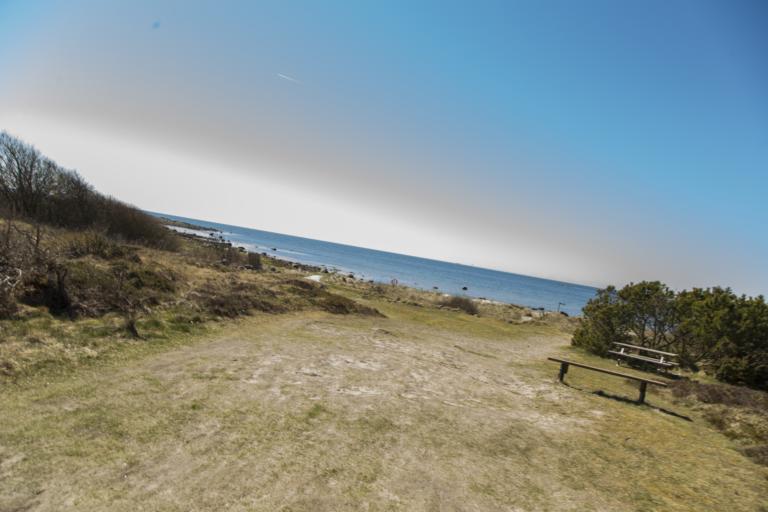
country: SE
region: Halland
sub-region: Varbergs Kommun
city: Traslovslage
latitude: 57.0459
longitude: 12.2874
